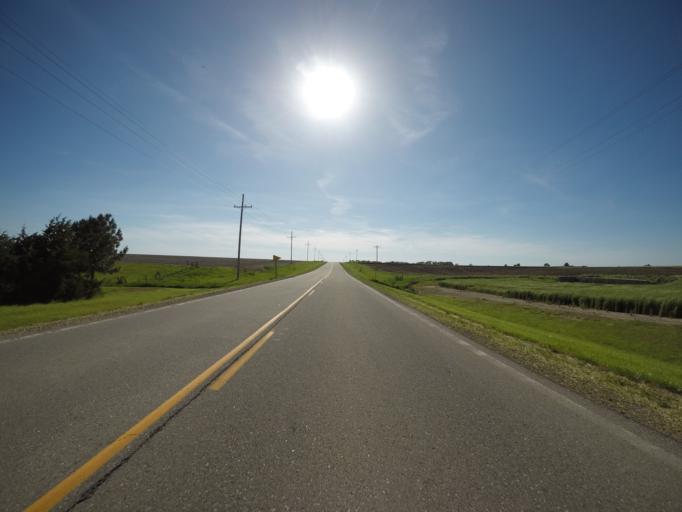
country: US
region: Kansas
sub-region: Clay County
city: Clay Center
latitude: 39.3646
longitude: -96.8907
